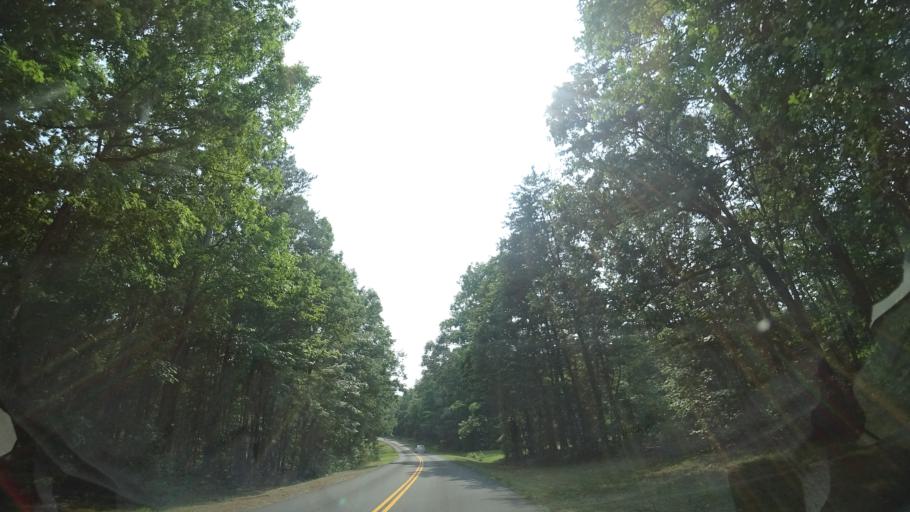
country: US
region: Virginia
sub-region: Louisa County
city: Louisa
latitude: 38.1429
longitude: -77.8156
